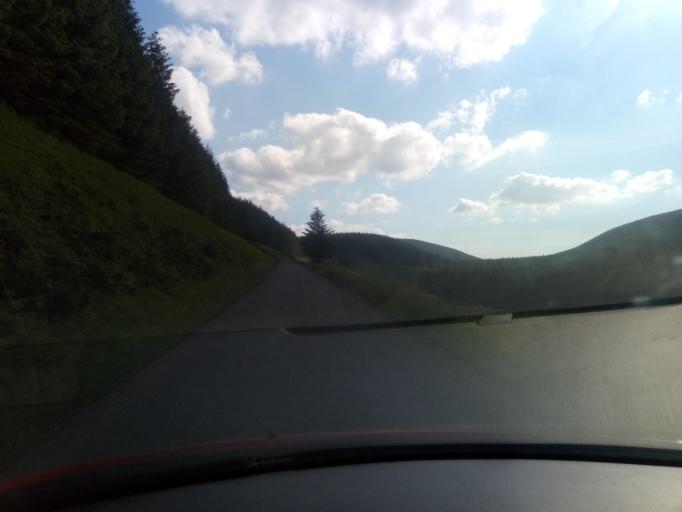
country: GB
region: Scotland
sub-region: The Scottish Borders
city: Innerleithen
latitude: 55.4741
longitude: -3.1426
